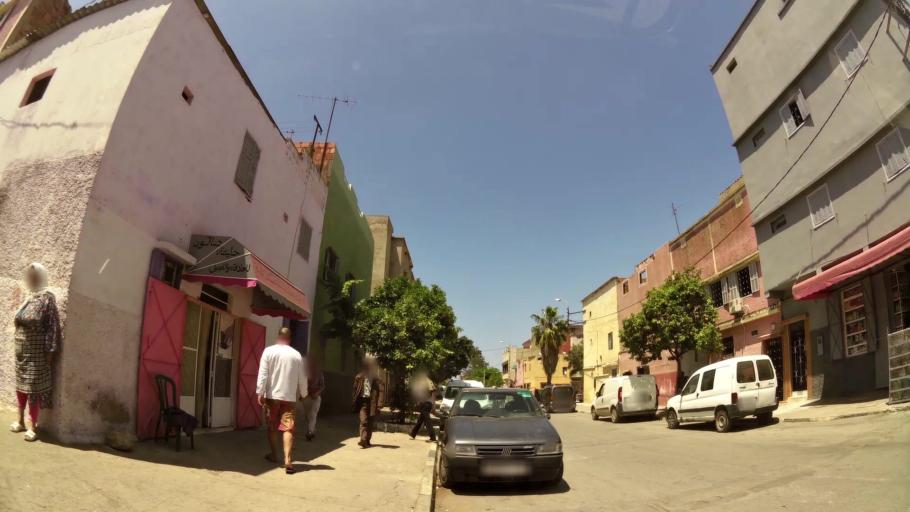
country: MA
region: Gharb-Chrarda-Beni Hssen
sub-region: Kenitra Province
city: Kenitra
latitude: 34.2569
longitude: -6.5594
